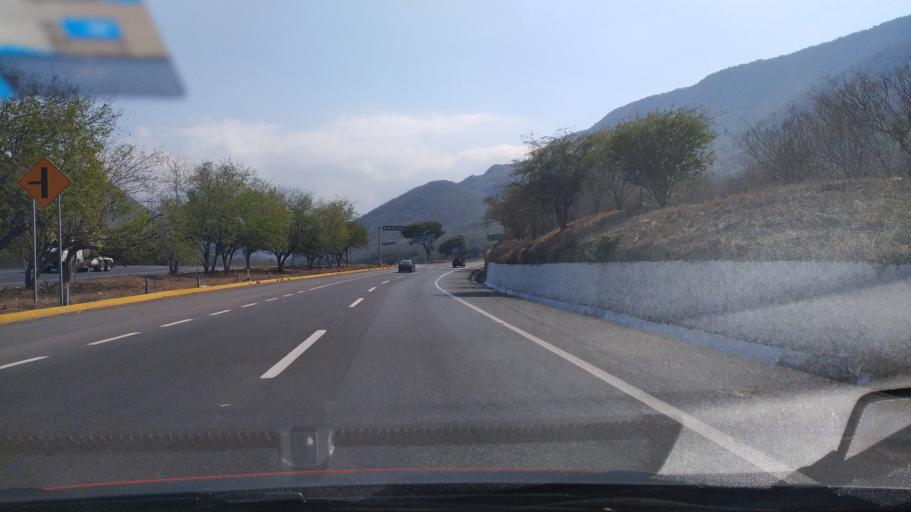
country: MX
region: Colima
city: Madrid
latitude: 19.1051
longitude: -103.7761
